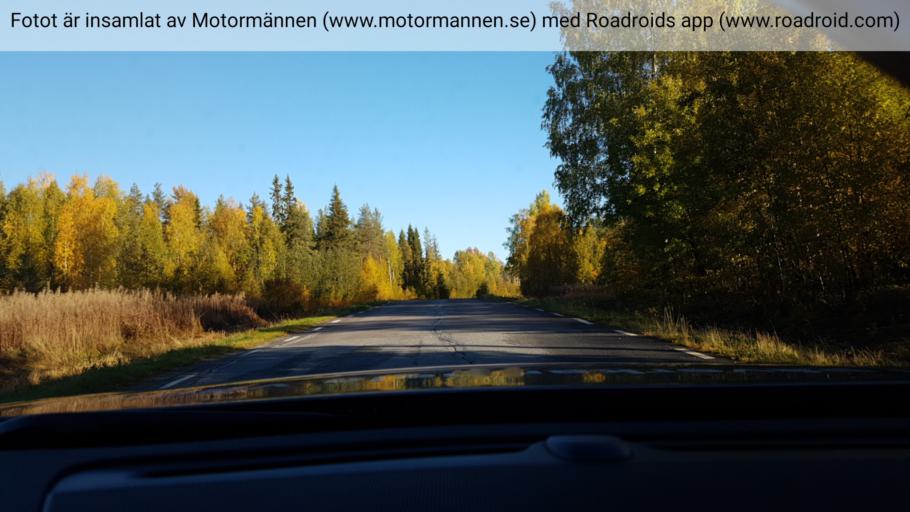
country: SE
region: Norrbotten
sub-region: Bodens Kommun
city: Boden
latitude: 65.9588
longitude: 21.5990
